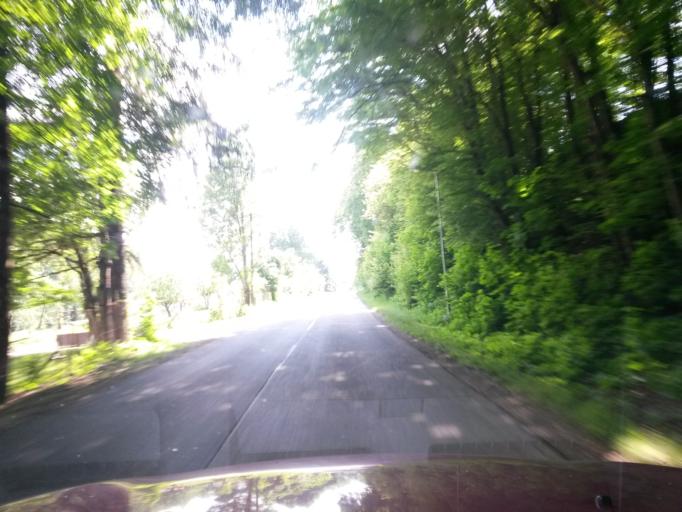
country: SK
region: Kosicky
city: Roznava
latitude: 48.6772
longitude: 20.5422
